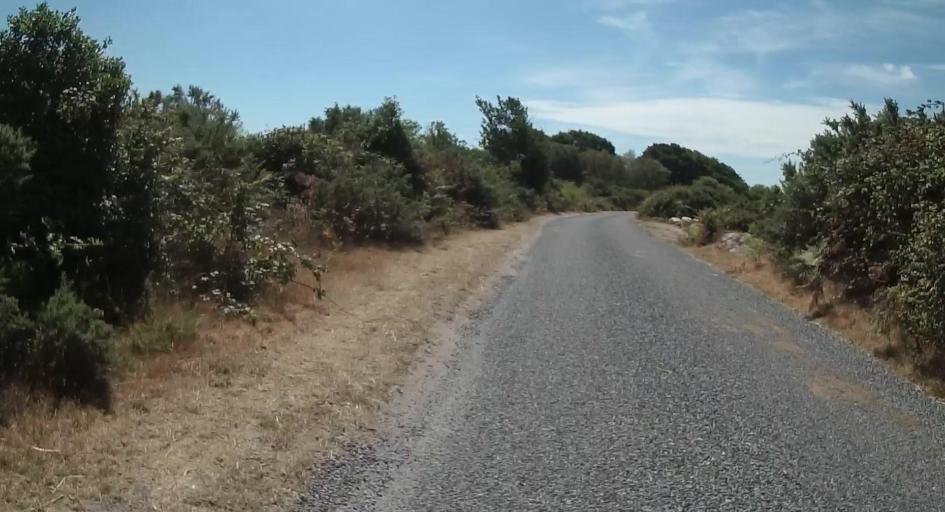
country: GB
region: England
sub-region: Dorset
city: Wareham
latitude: 50.6583
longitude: -2.0564
